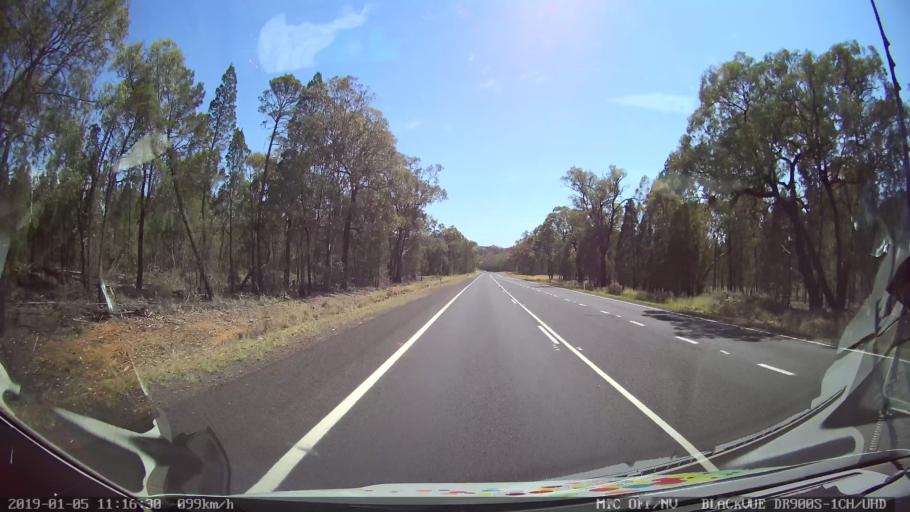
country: AU
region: New South Wales
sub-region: Warrumbungle Shire
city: Coonabarabran
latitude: -31.3379
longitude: 149.2987
